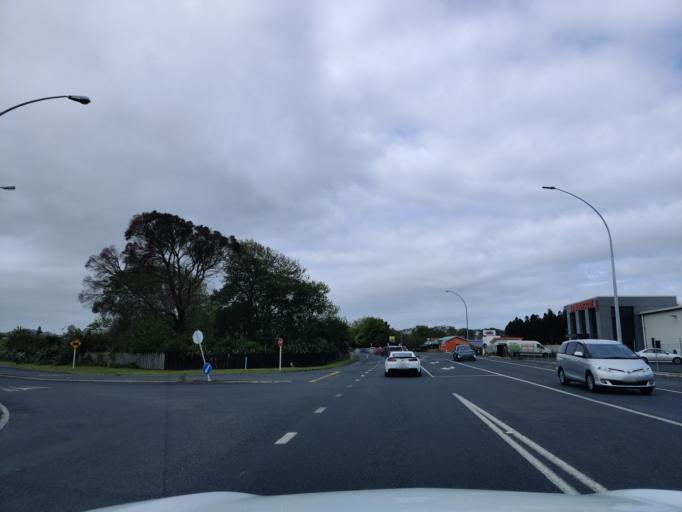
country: NZ
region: Waikato
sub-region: Waikato District
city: Te Kauwhata
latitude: -37.5278
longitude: 175.1595
